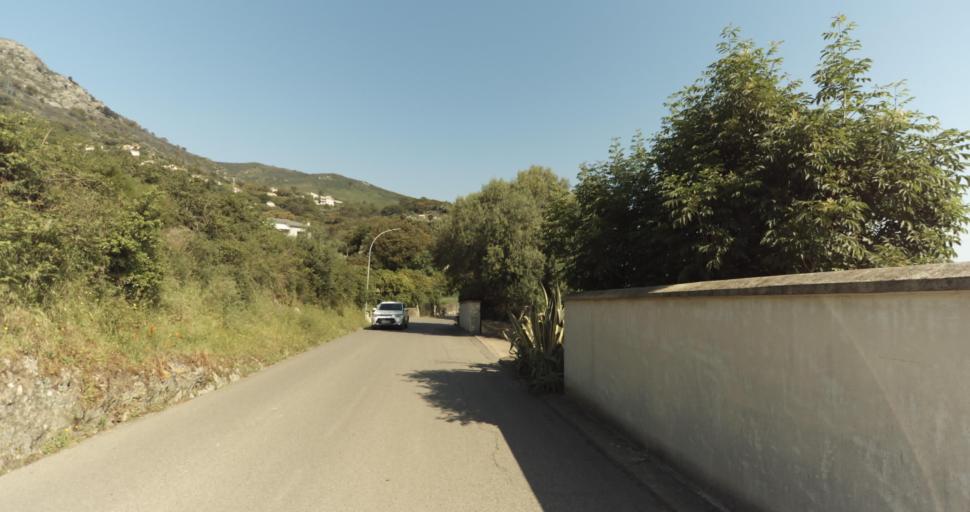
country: FR
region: Corsica
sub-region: Departement de la Haute-Corse
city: Biguglia
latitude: 42.6280
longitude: 9.4239
